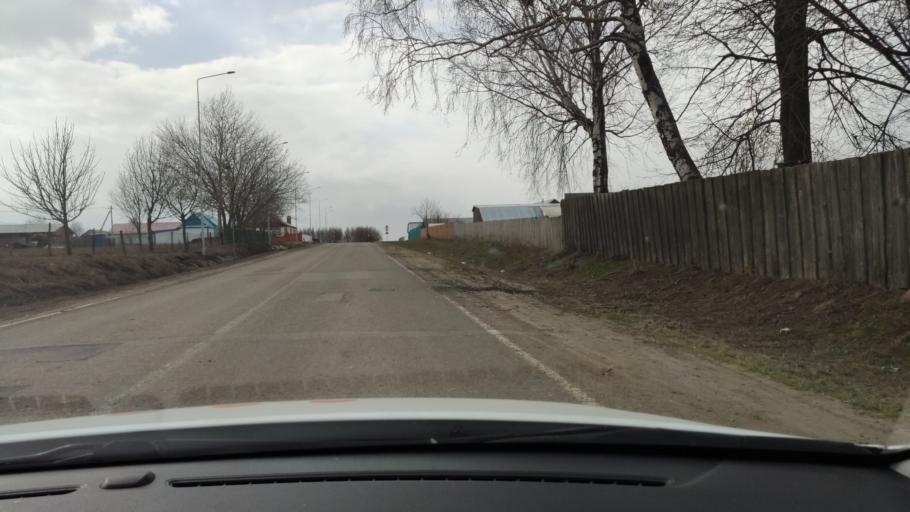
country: RU
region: Tatarstan
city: Vysokaya Gora
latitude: 56.2188
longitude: 49.2584
